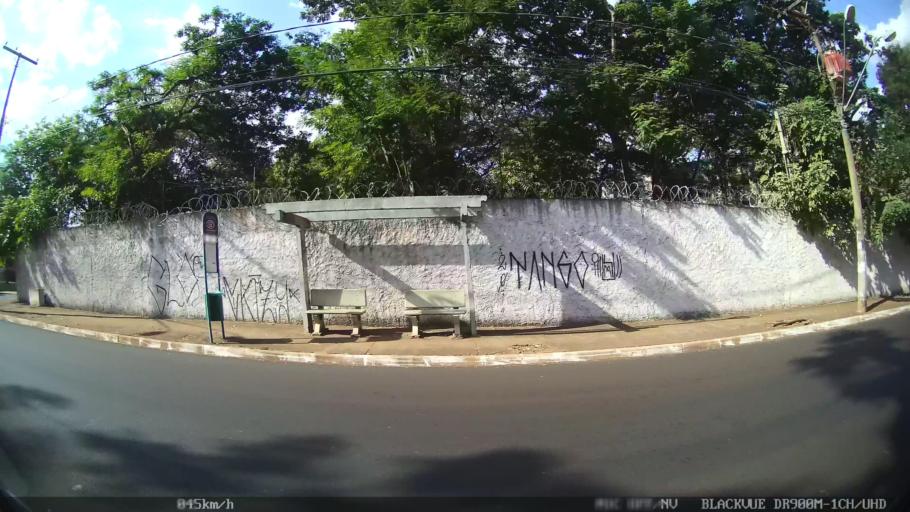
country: BR
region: Sao Paulo
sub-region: Ribeirao Preto
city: Ribeirao Preto
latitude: -21.1914
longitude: -47.8245
